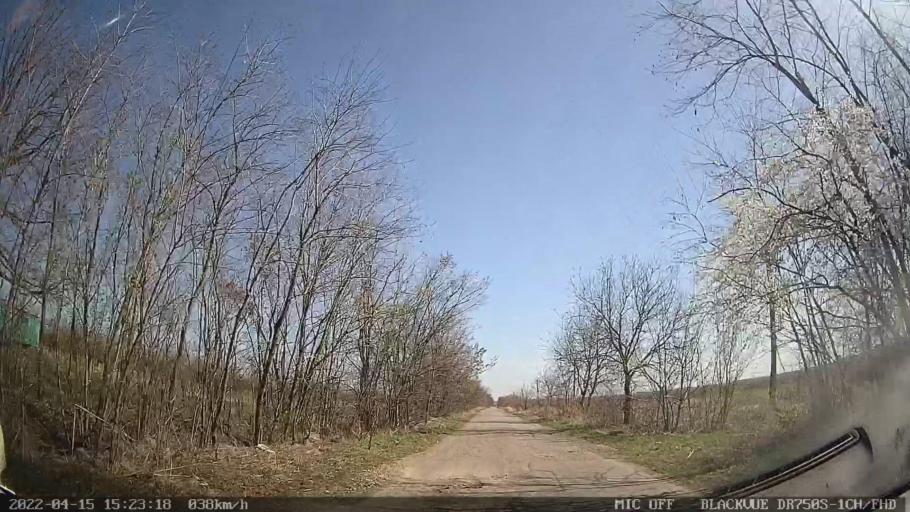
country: MD
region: Raionul Ocnita
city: Otaci
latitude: 48.3758
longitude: 27.9187
